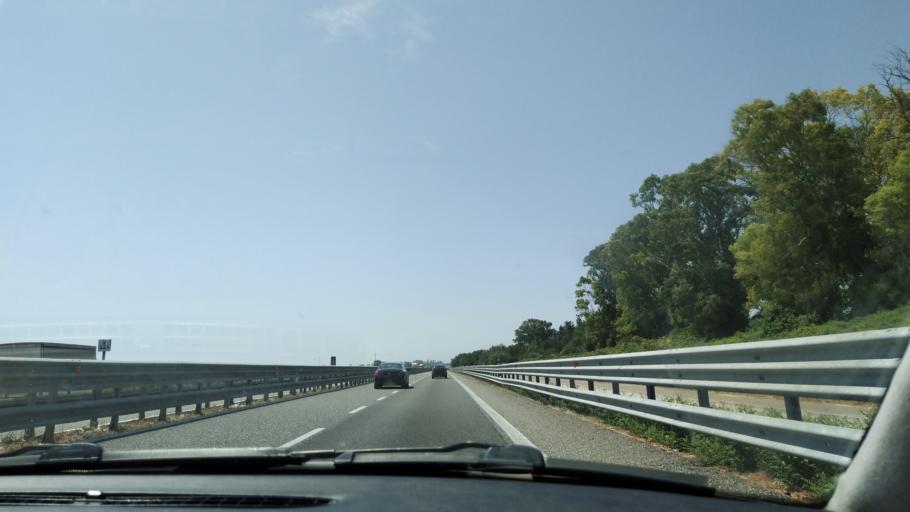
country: IT
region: Basilicate
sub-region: Provincia di Matera
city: Marconia
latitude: 40.3502
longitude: 16.7696
